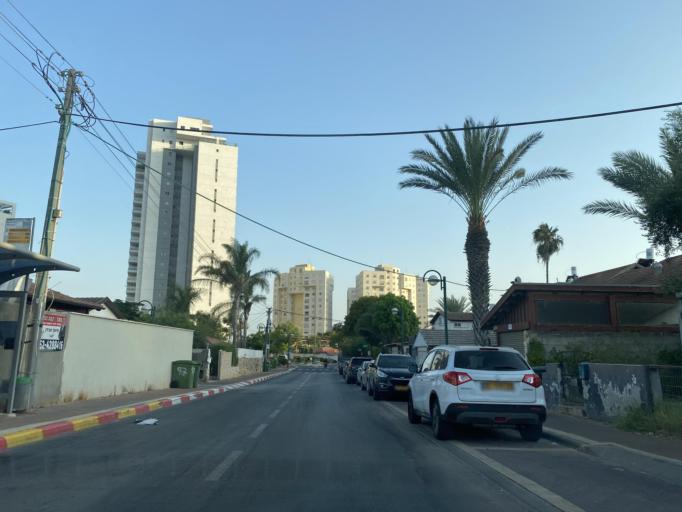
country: IL
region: Tel Aviv
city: Ramat HaSharon
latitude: 32.1333
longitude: 34.8625
